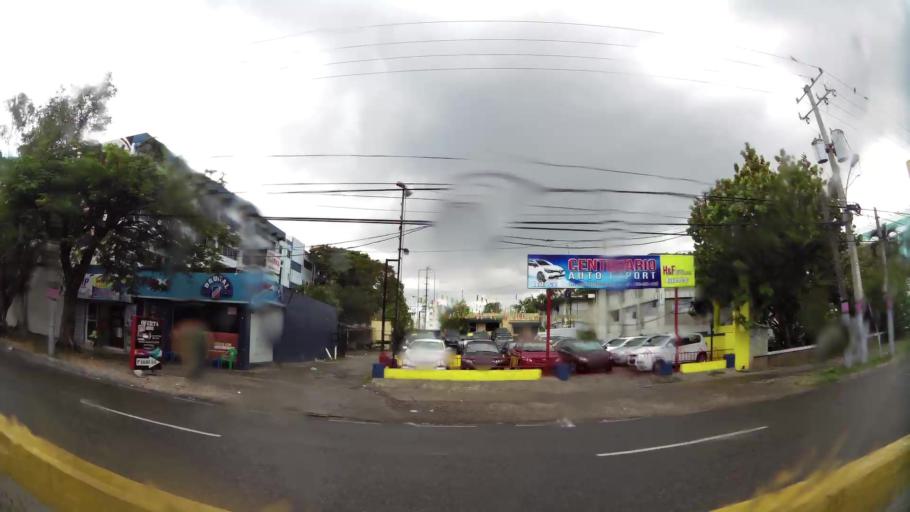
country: DO
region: Nacional
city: Ciudad Nueva
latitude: 18.4747
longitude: -69.9131
